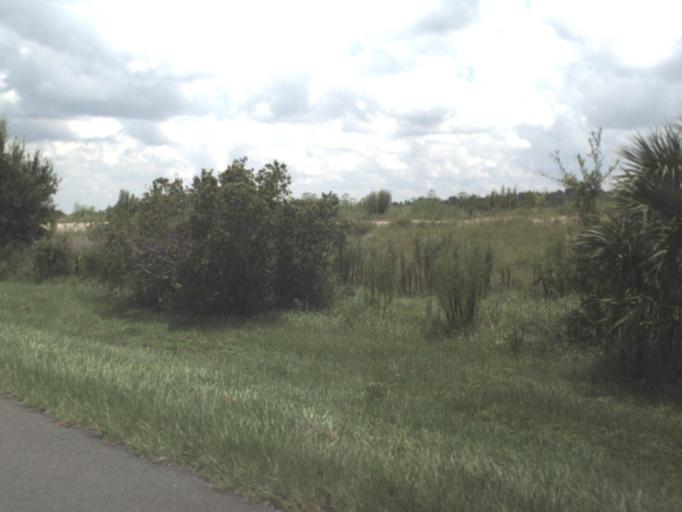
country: US
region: Florida
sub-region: Hillsborough County
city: Balm
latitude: 27.7045
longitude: -82.1307
